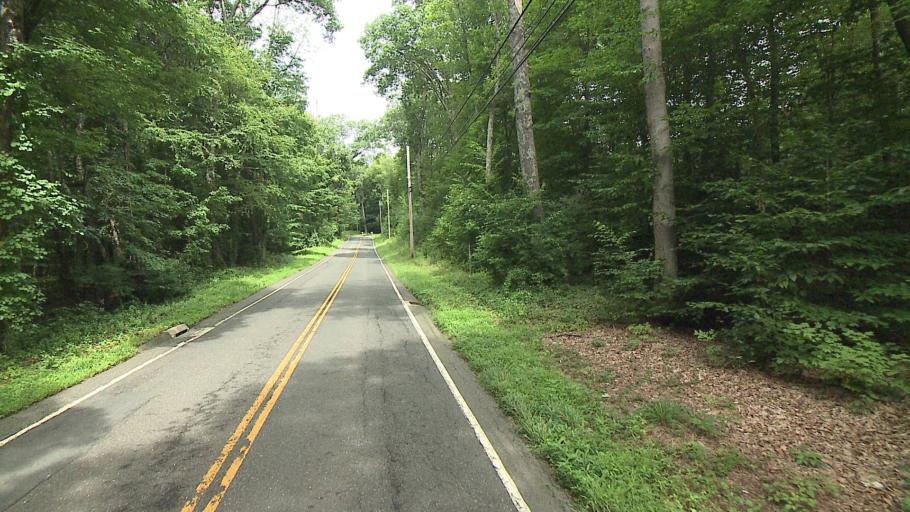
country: US
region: Connecticut
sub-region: Litchfield County
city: Woodbury
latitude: 41.5509
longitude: -73.2449
